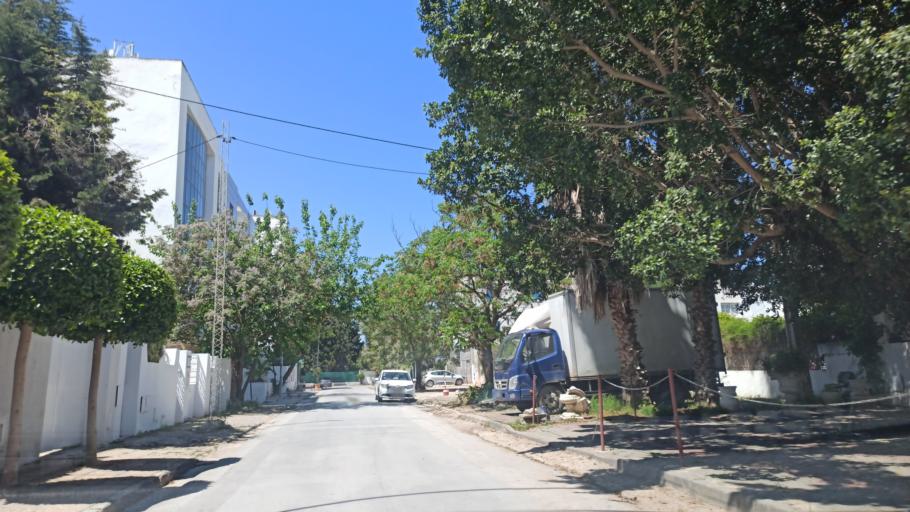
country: TN
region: Tunis
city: Tunis
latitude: 36.8248
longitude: 10.1832
